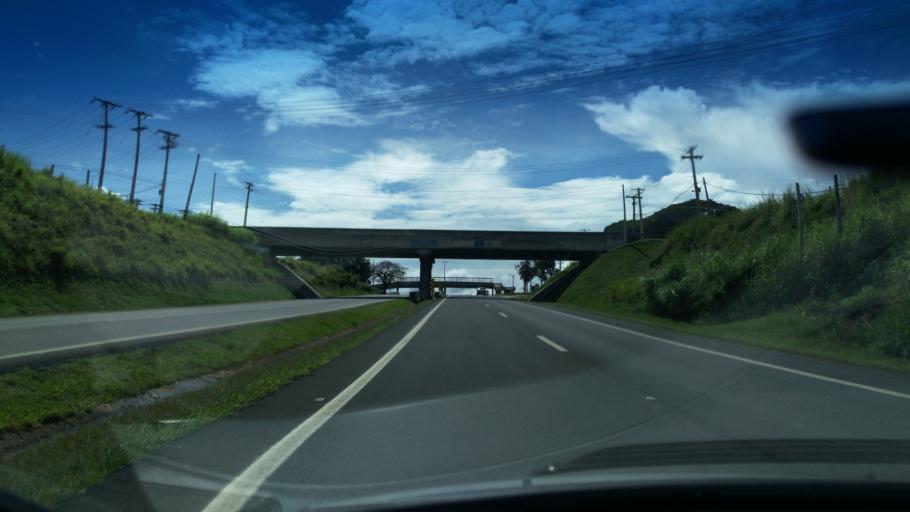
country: BR
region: Sao Paulo
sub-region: Santo Antonio Do Jardim
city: Espirito Santo do Pinhal
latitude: -22.1943
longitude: -46.7726
